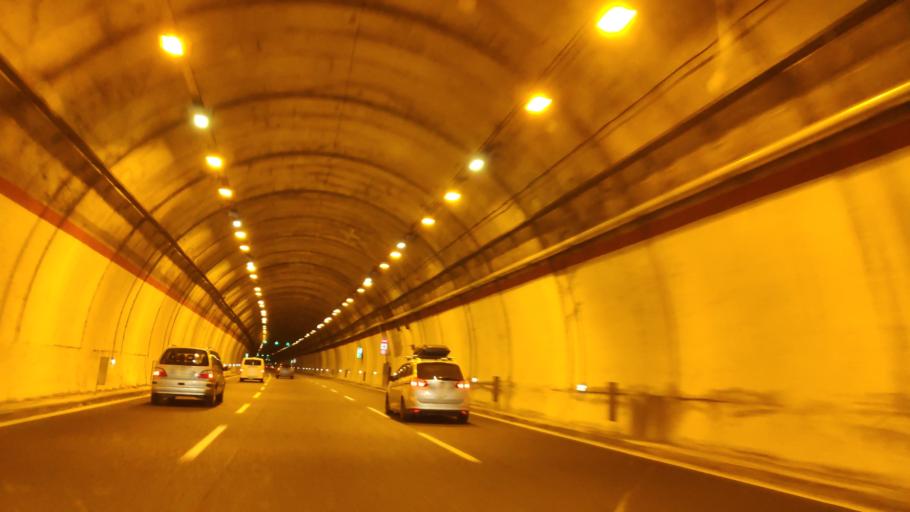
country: IT
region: Campania
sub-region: Provincia di Salerno
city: Serre
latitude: 40.6248
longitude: 15.1799
